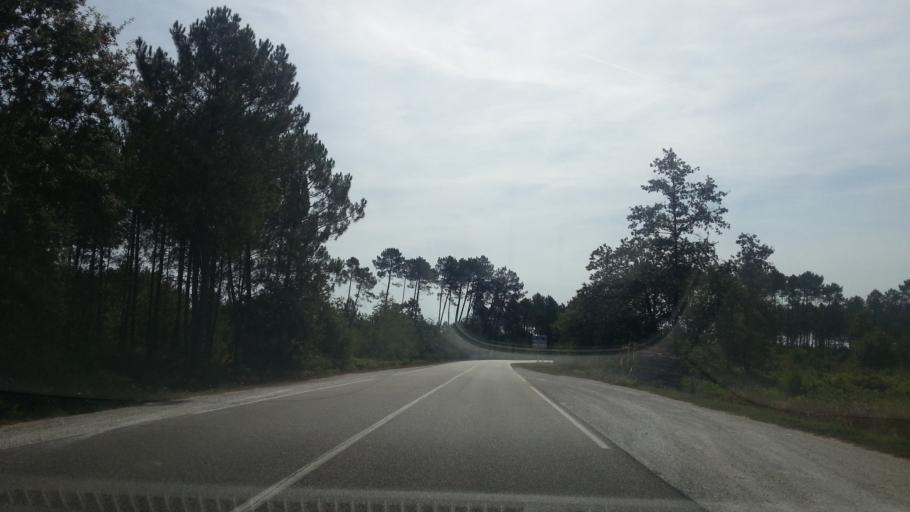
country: FR
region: Aquitaine
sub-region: Departement de la Gironde
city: Illats
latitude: 44.6114
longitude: -0.3691
